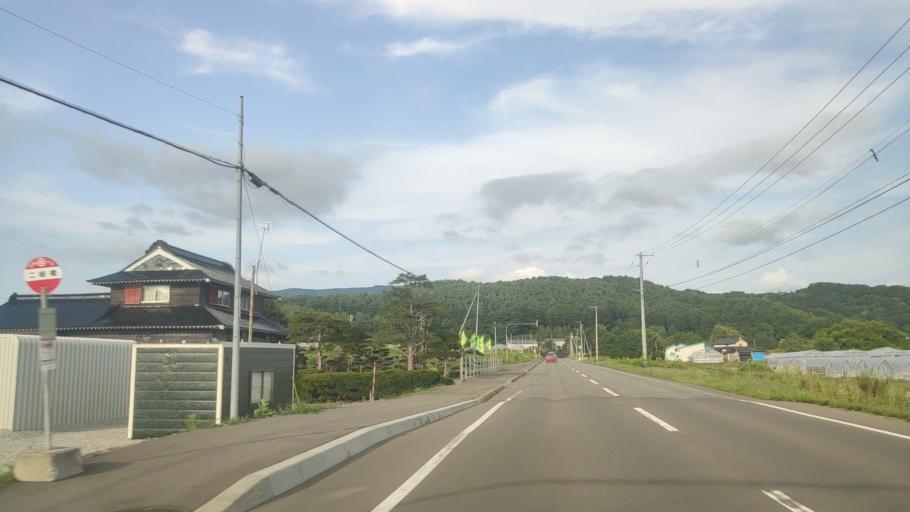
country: JP
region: Hokkaido
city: Iwamizawa
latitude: 43.0415
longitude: 141.9061
